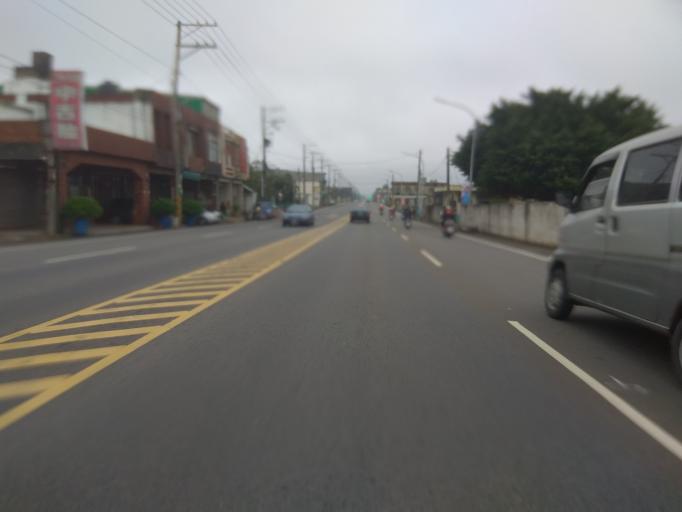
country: TW
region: Taiwan
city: Taoyuan City
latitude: 25.0230
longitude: 121.1166
